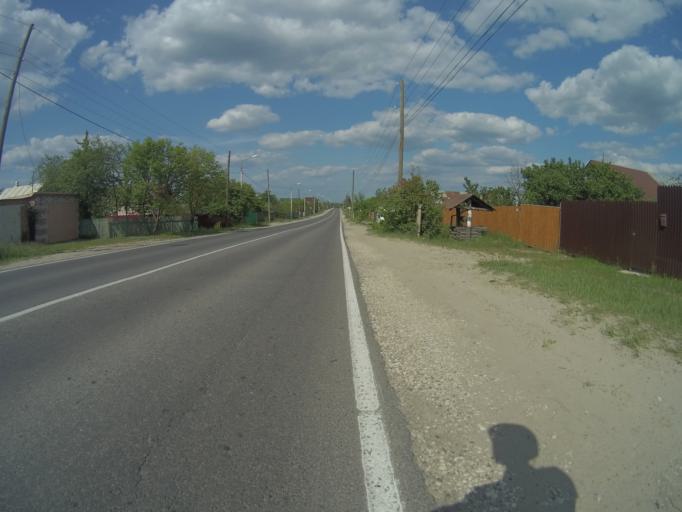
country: RU
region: Vladimir
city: Raduzhnyy
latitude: 56.0132
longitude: 40.3107
